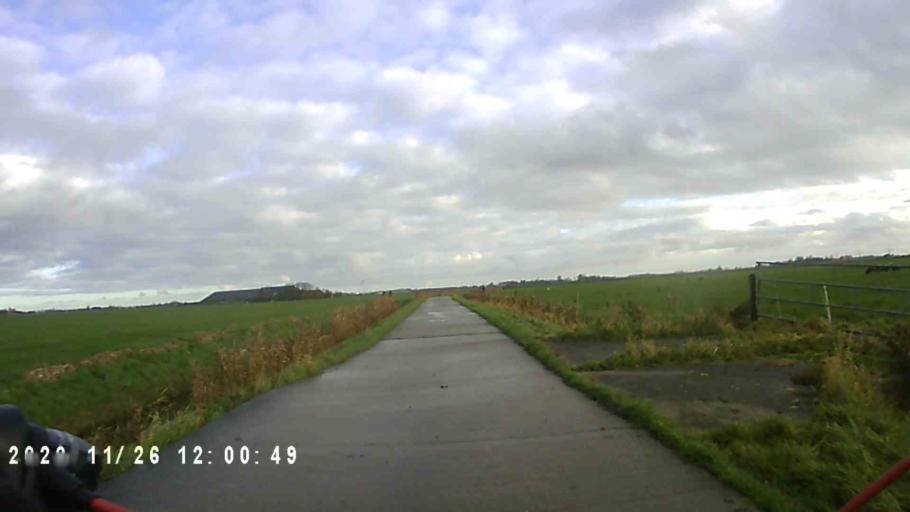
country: NL
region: Groningen
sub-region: Gemeente Bedum
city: Bedum
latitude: 53.3195
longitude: 6.6087
